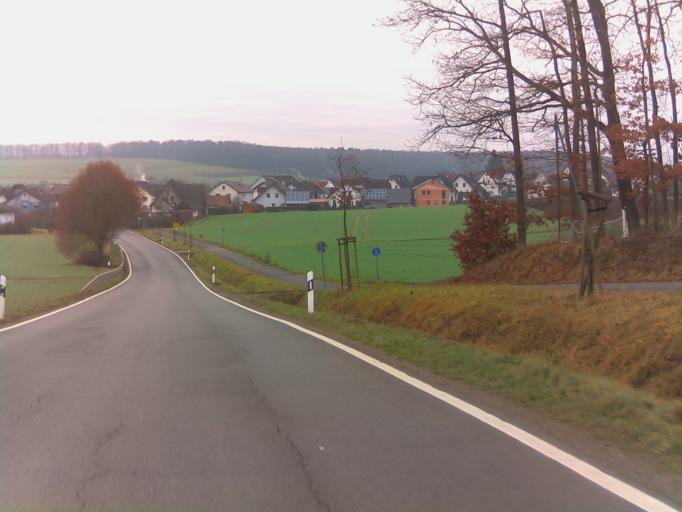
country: DE
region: Bavaria
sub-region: Regierungsbezirk Unterfranken
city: Schonau
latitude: 50.0782
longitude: 9.7510
